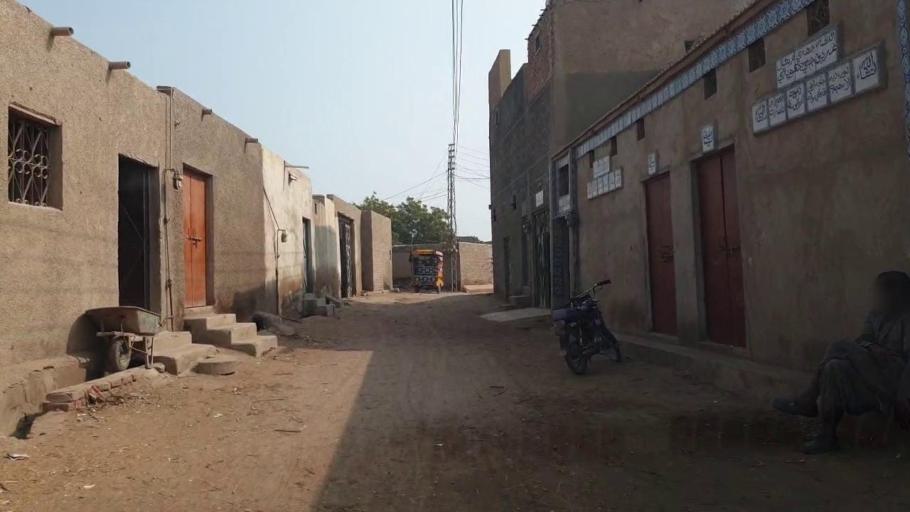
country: PK
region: Sindh
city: Bhit Shah
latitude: 25.8359
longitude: 68.4649
